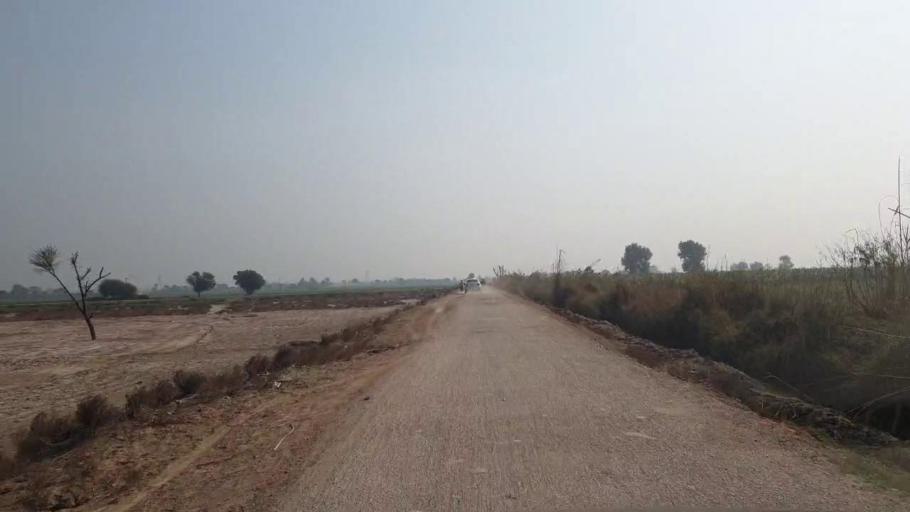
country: PK
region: Sindh
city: Hala
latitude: 25.9454
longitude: 68.4319
